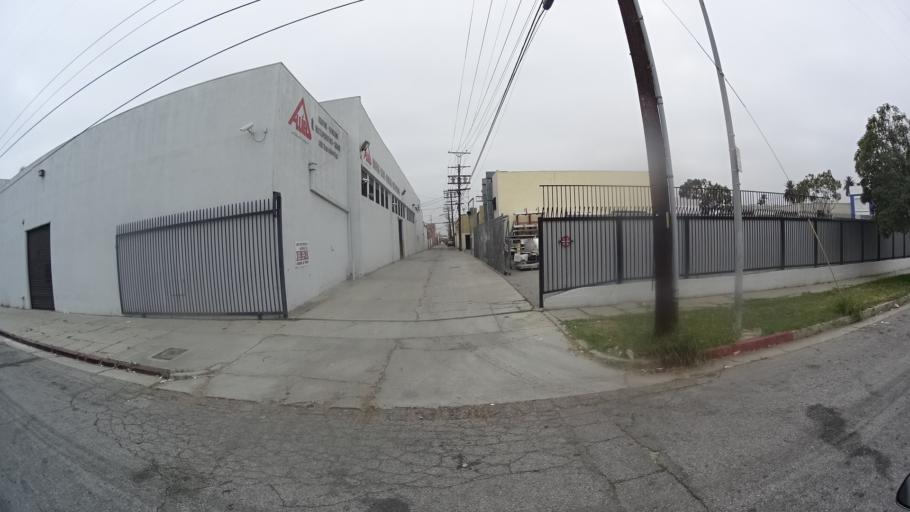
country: US
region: California
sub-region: Los Angeles County
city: View Park-Windsor Hills
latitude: 34.0250
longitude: -118.3484
